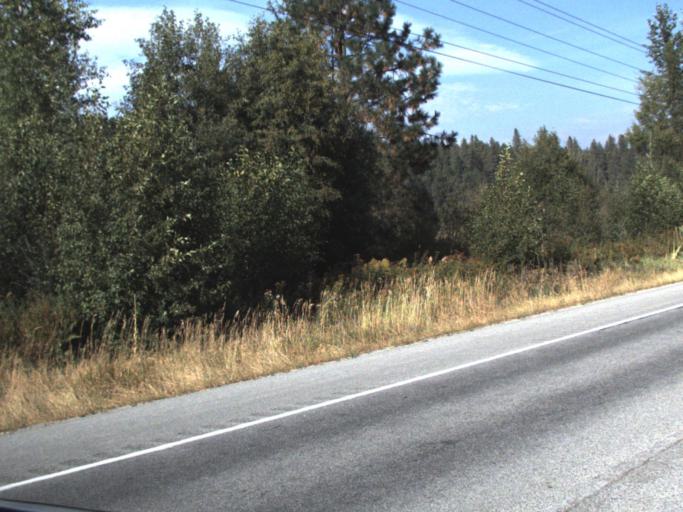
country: US
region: Washington
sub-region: Pend Oreille County
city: Newport
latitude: 48.1697
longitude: -117.0753
